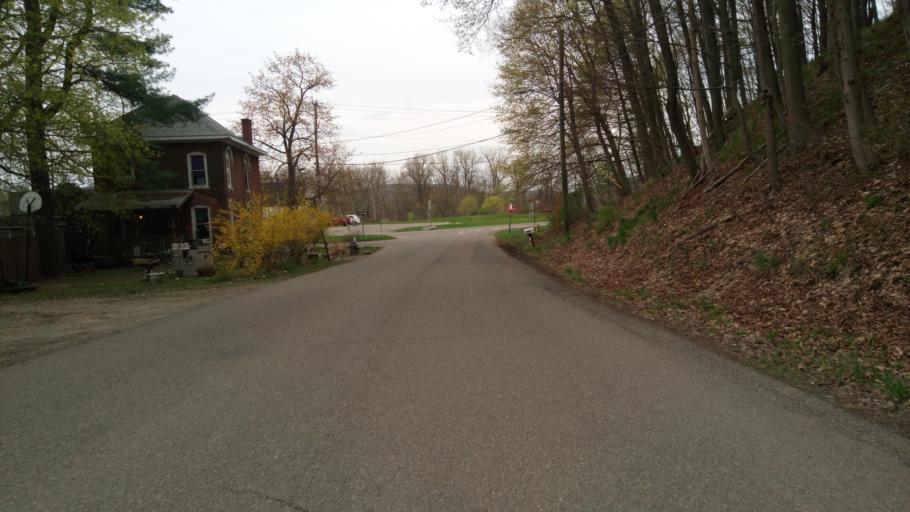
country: US
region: New York
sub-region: Chemung County
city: Southport
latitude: 42.0155
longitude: -76.7260
